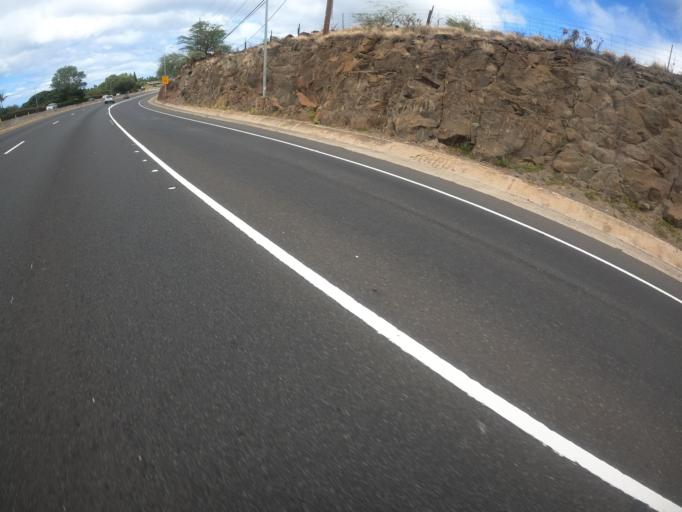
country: US
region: Hawaii
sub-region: Honolulu County
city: Makakilo City
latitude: 21.3444
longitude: -158.1195
